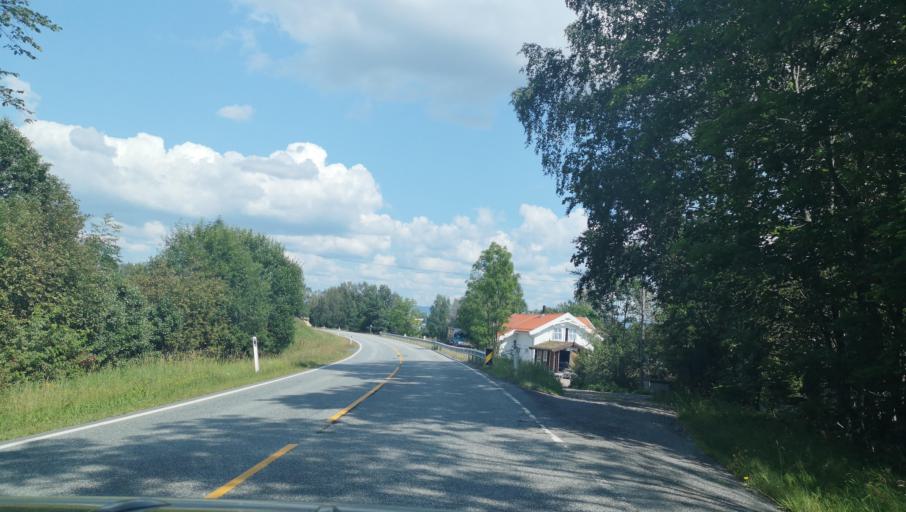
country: NO
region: Buskerud
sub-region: Ovre Eiker
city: Hokksund
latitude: 59.7093
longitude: 9.8164
